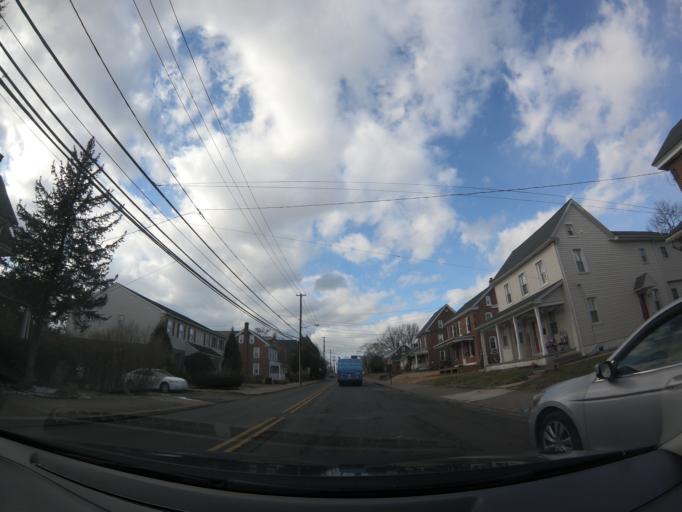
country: US
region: Pennsylvania
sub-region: Montgomery County
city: Telford
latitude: 40.3268
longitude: -75.3310
